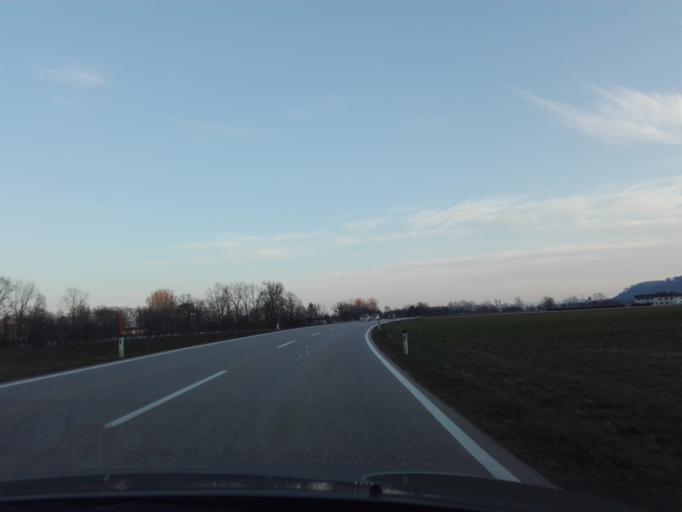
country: AT
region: Upper Austria
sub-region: Politischer Bezirk Urfahr-Umgebung
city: Feldkirchen an der Donau
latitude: 48.3680
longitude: 13.9822
